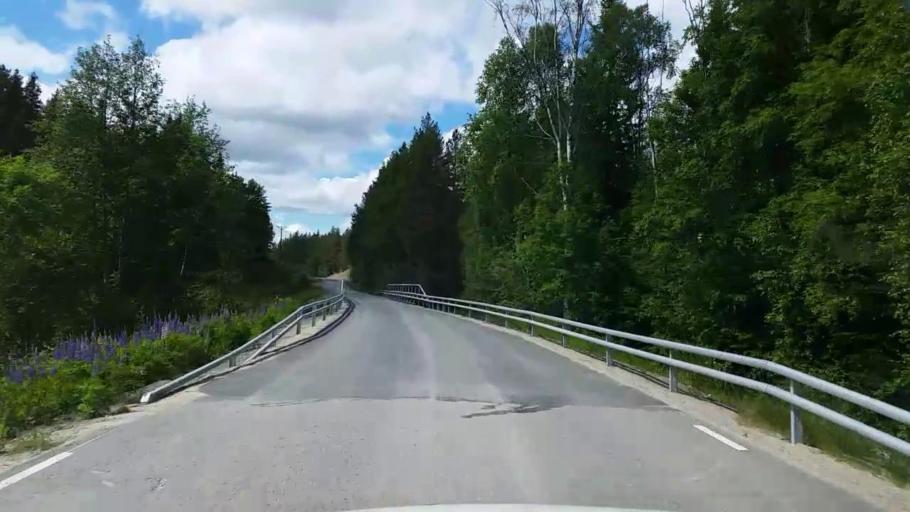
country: SE
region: Gaevleborg
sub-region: Bollnas Kommun
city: Vittsjo
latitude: 61.0676
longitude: 16.2985
